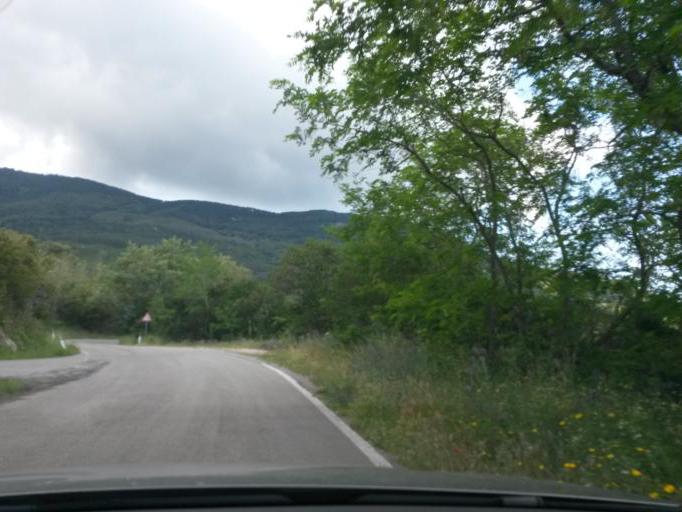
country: IT
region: Tuscany
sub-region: Provincia di Livorno
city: Campo nell'Elba
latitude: 42.7603
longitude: 10.2116
